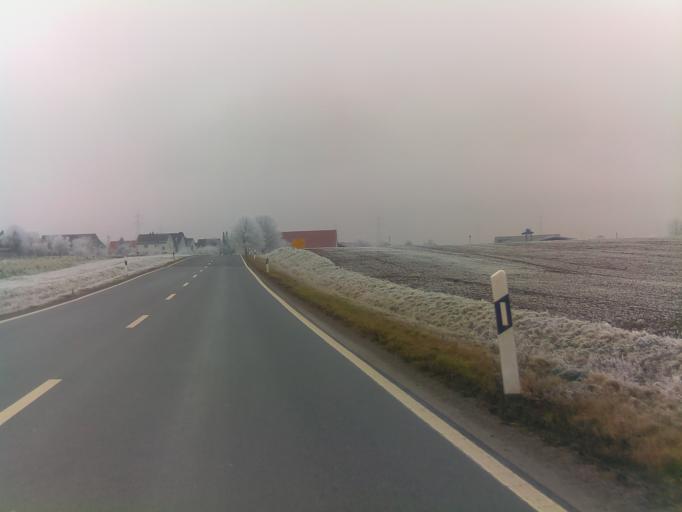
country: DE
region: Bavaria
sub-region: Regierungsbezirk Unterfranken
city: Giebelstadt
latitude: 49.6154
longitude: 9.9559
